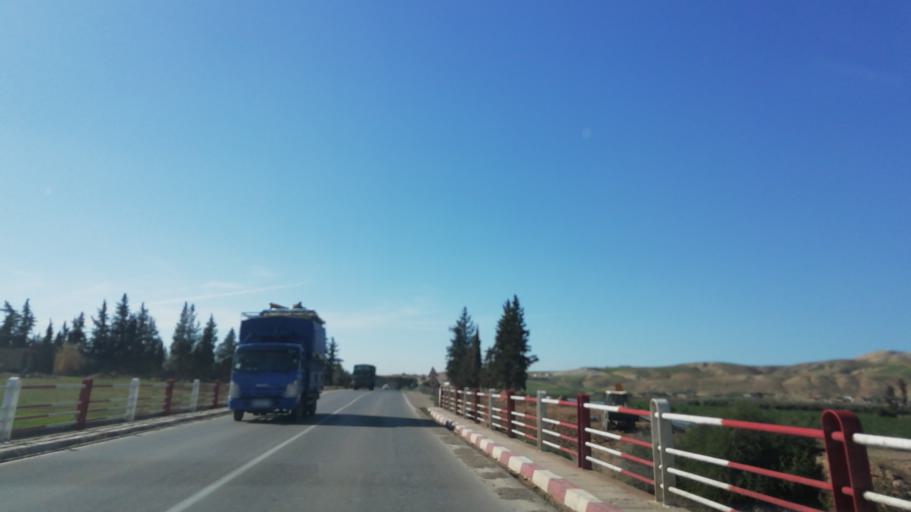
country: DZ
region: Mascara
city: Oued el Abtal
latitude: 35.4576
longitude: 0.7547
